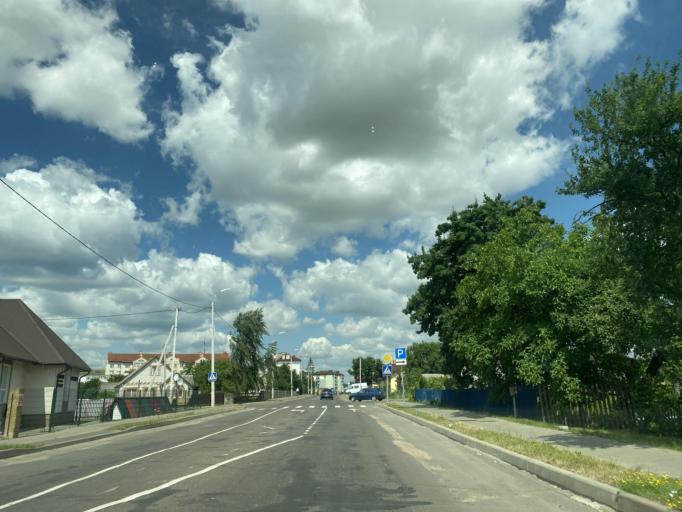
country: BY
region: Brest
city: Ivanava
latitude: 52.1450
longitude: 25.5422
